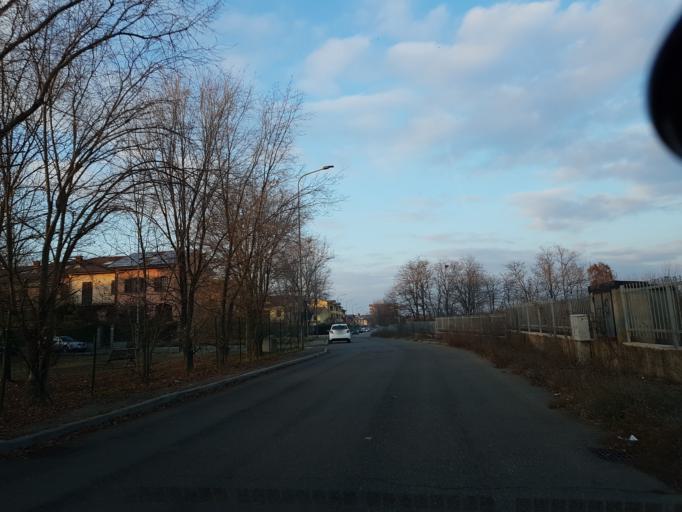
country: IT
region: Piedmont
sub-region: Provincia di Alessandria
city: Novi Ligure
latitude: 44.7571
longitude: 8.8059
